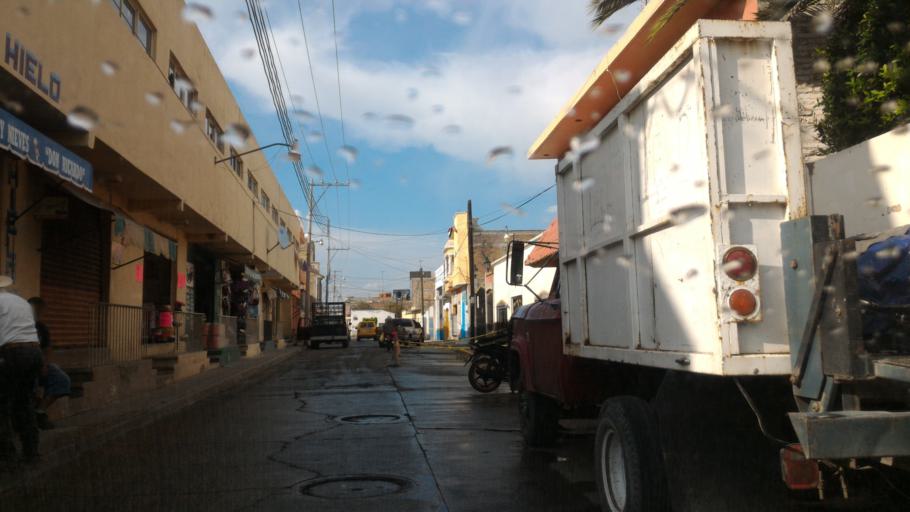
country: MX
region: Guanajuato
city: Ciudad Manuel Doblado
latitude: 20.7255
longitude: -101.9500
